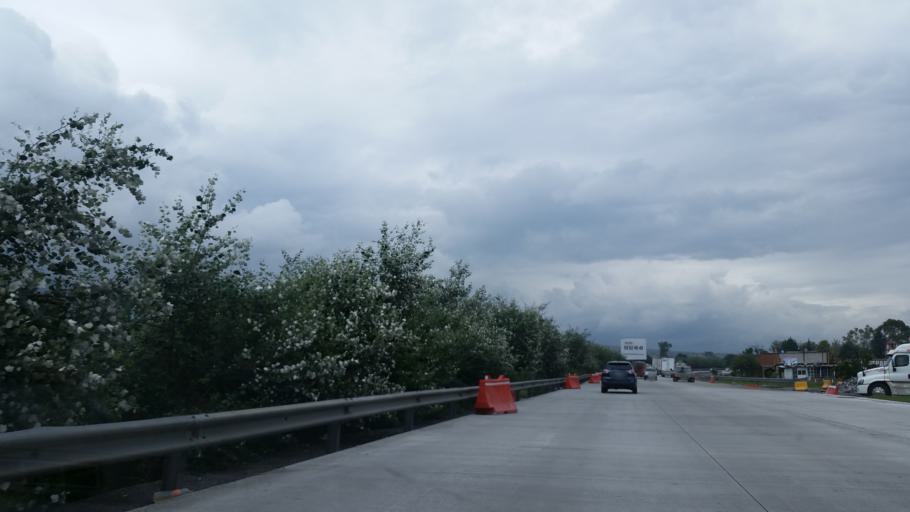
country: MX
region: Mexico
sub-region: Huehuetoca
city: Villa URBI del Rey
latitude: 19.8338
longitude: -99.2691
